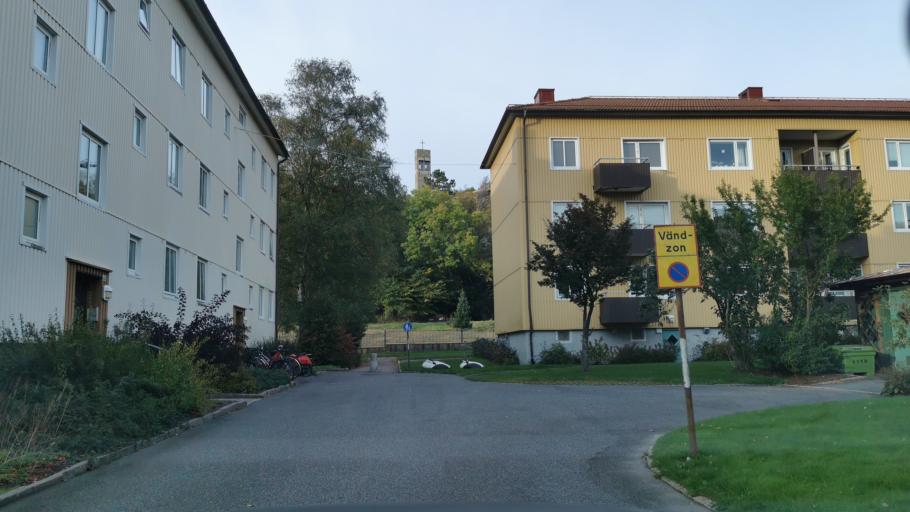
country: SE
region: Vaestra Goetaland
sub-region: Goteborg
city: Eriksbo
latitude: 57.7341
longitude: 12.0173
